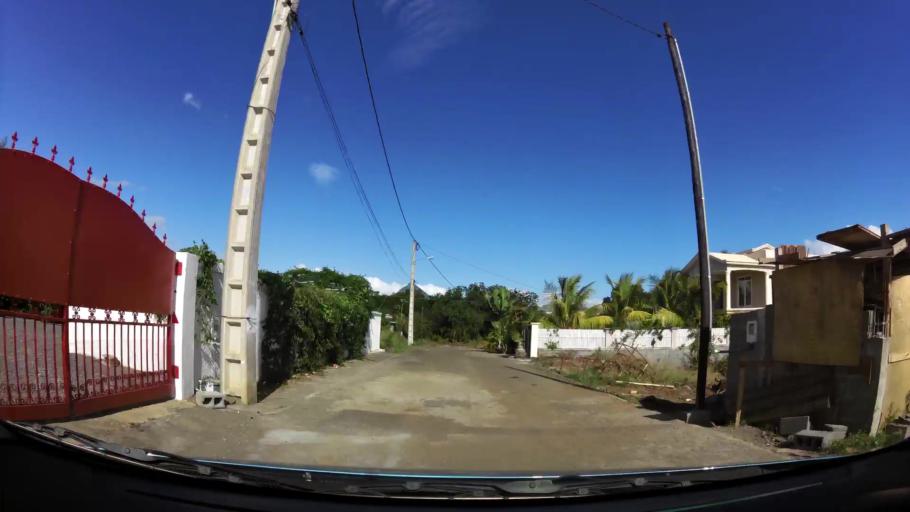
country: MU
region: Black River
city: Albion
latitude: -20.2066
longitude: 57.4117
